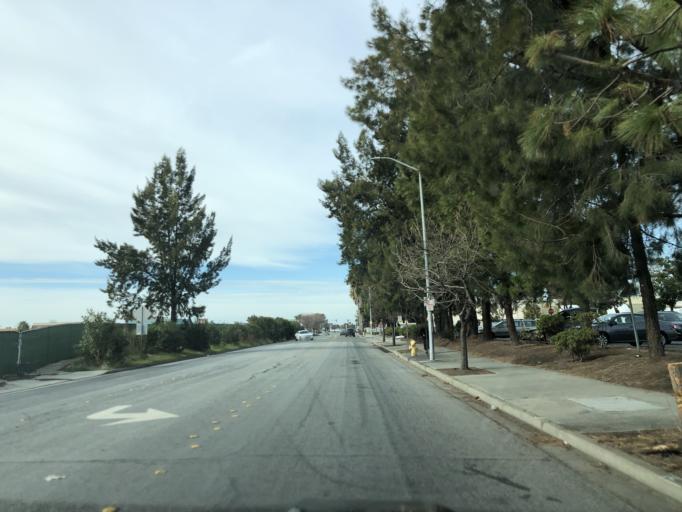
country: US
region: California
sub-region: Alameda County
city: Fremont
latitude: 37.5189
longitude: -121.9862
